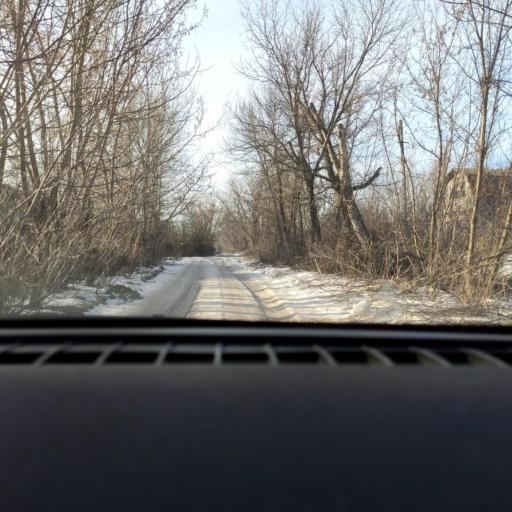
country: RU
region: Voronezj
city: Maslovka
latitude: 51.6125
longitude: 39.2735
